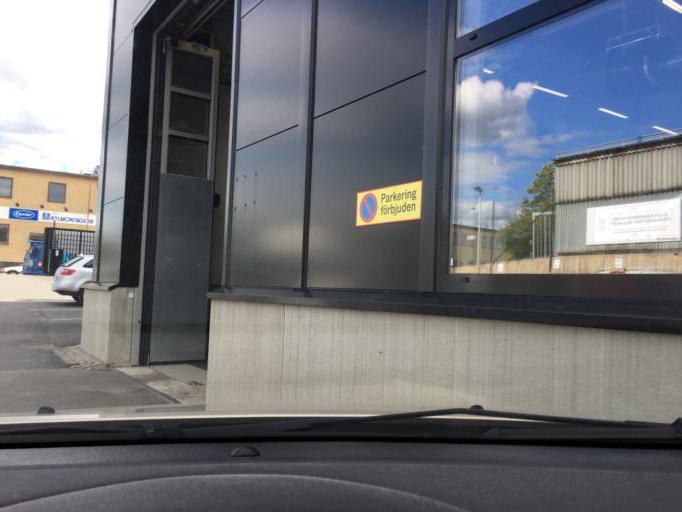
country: SE
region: Stockholm
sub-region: Stockholms Kommun
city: Arsta
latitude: 59.2603
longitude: 18.0556
